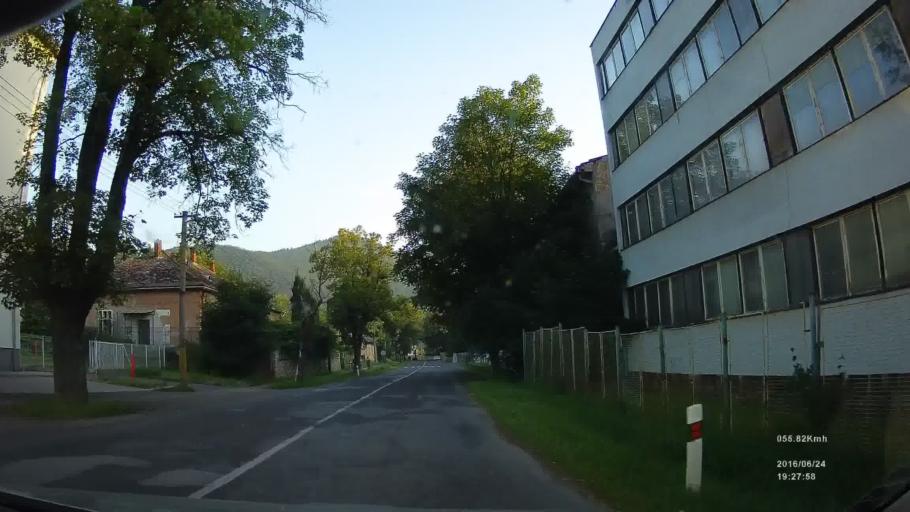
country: SK
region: Banskobystricky
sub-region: Okres Banska Bystrica
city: Brezno
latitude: 48.8117
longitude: 19.5573
